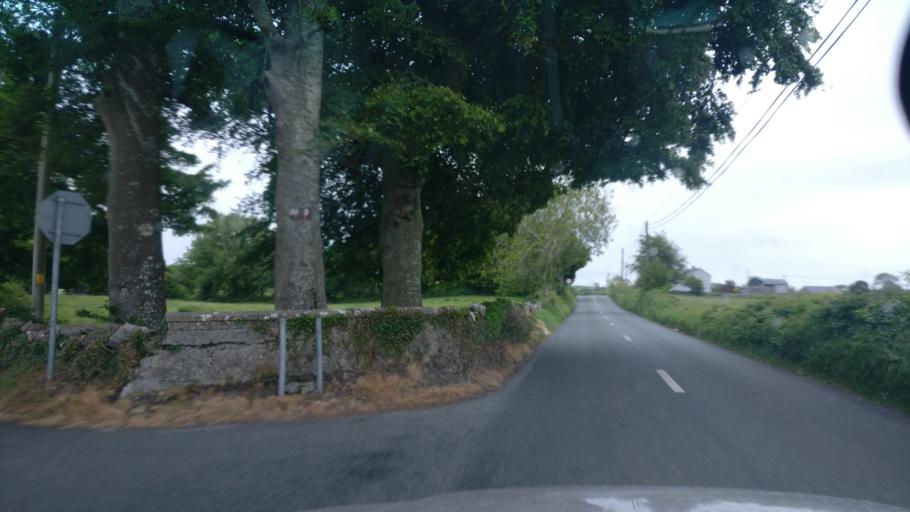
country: IE
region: Connaught
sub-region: County Galway
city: Gort
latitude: 53.0662
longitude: -8.7766
